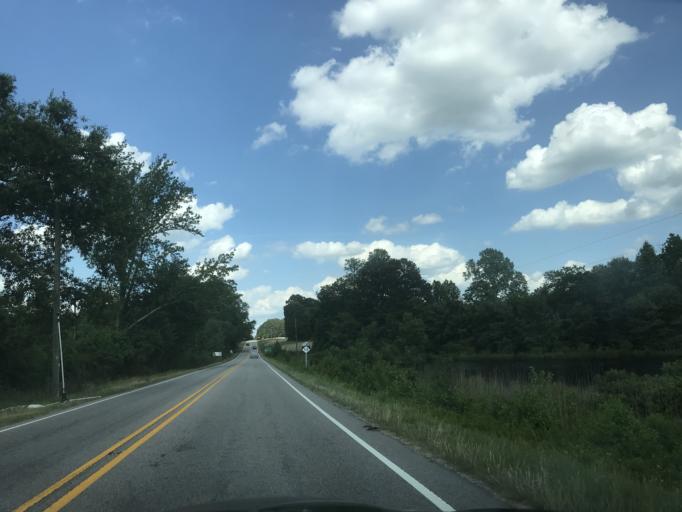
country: US
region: North Carolina
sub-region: Wake County
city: Rolesville
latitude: 35.9689
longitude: -78.3984
